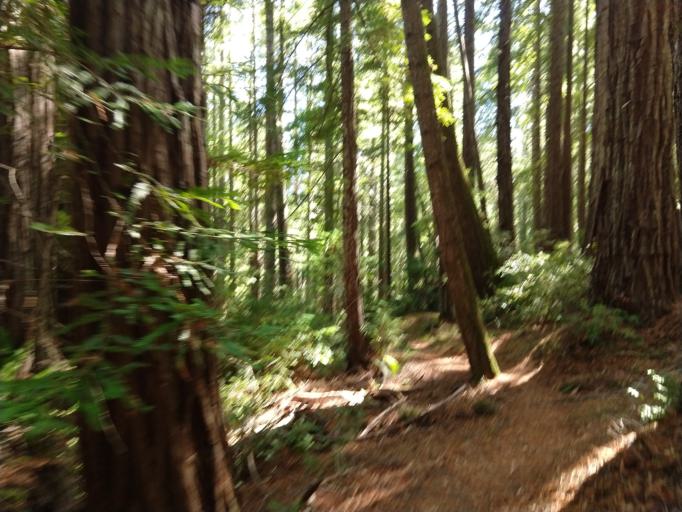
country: US
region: California
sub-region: Humboldt County
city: Rio Dell
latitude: 40.3574
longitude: -123.9945
